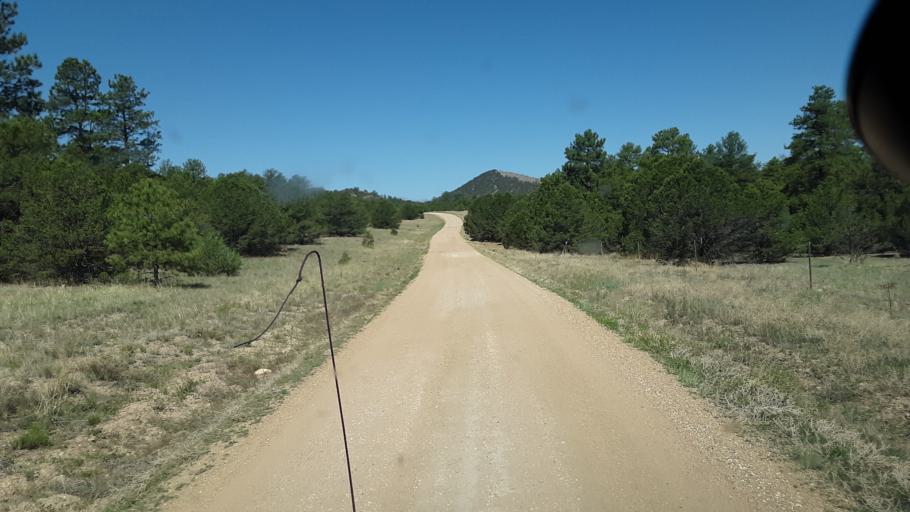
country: US
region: Colorado
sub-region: Custer County
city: Westcliffe
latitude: 38.2943
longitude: -105.4685
